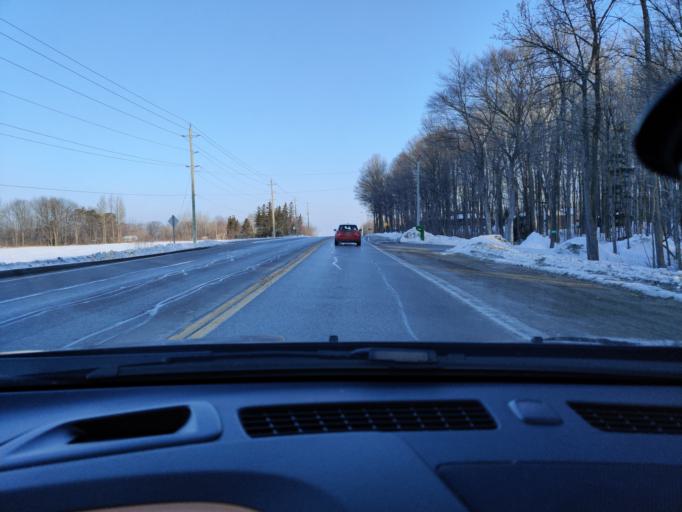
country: CA
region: Ontario
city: Angus
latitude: 44.3940
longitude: -79.7984
